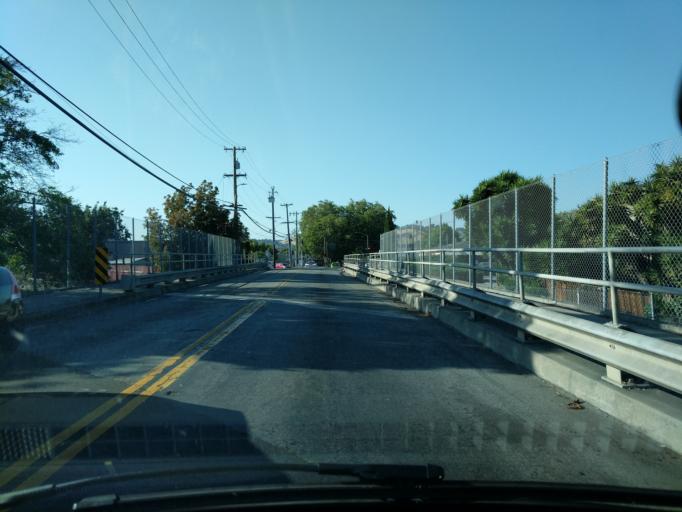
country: US
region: California
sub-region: Alameda County
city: San Lorenzo
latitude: 37.6854
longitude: -122.1168
